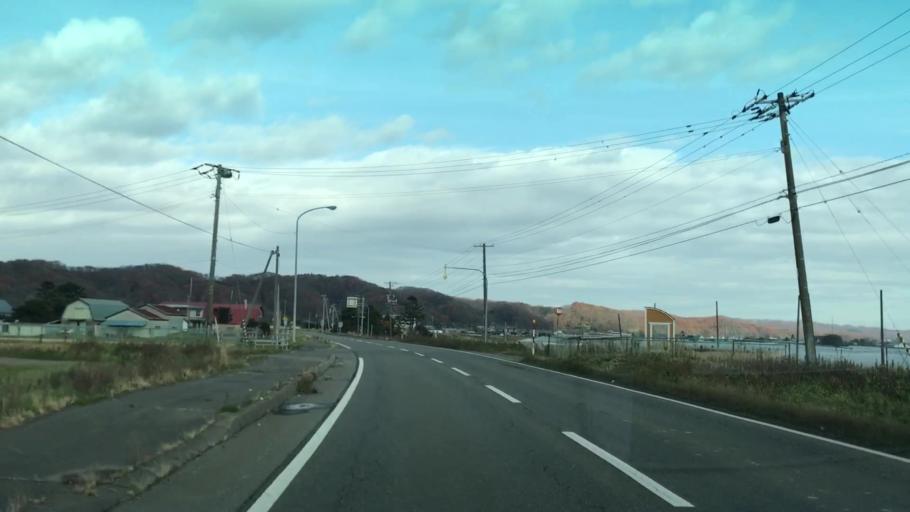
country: JP
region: Hokkaido
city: Shizunai-furukawacho
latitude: 42.5370
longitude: 142.0555
